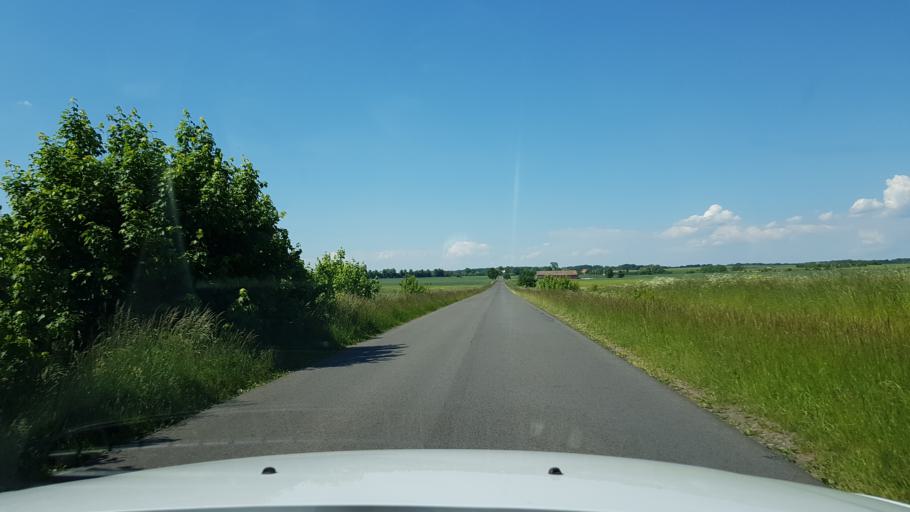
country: PL
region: West Pomeranian Voivodeship
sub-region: Powiat gryfinski
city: Banie
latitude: 53.0691
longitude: 14.6223
